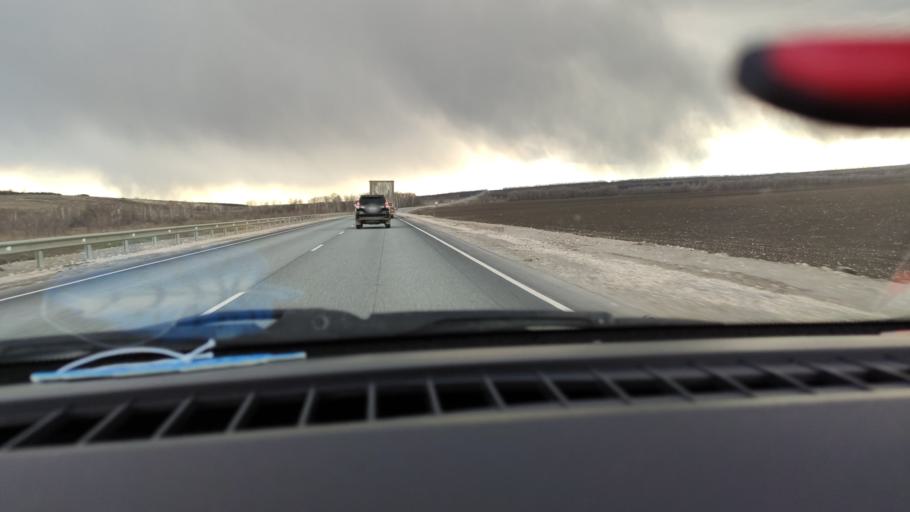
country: RU
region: Saratov
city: Yelshanka
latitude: 51.8559
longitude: 46.4941
